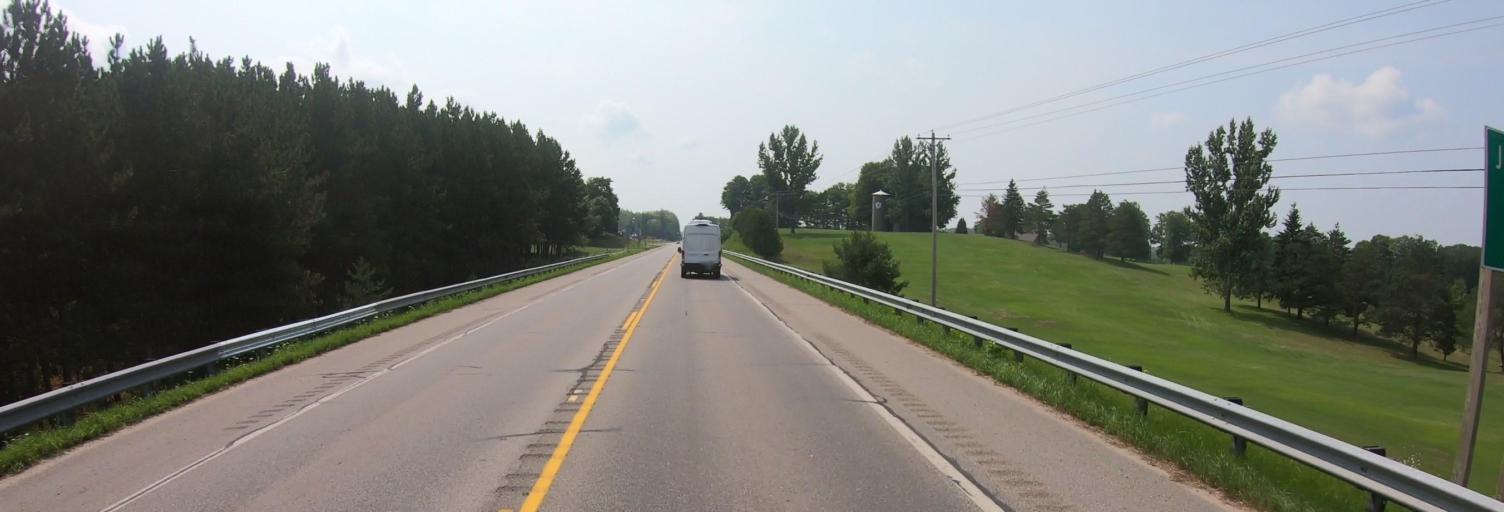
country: US
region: Michigan
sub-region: Luce County
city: Newberry
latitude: 46.3076
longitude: -85.5096
